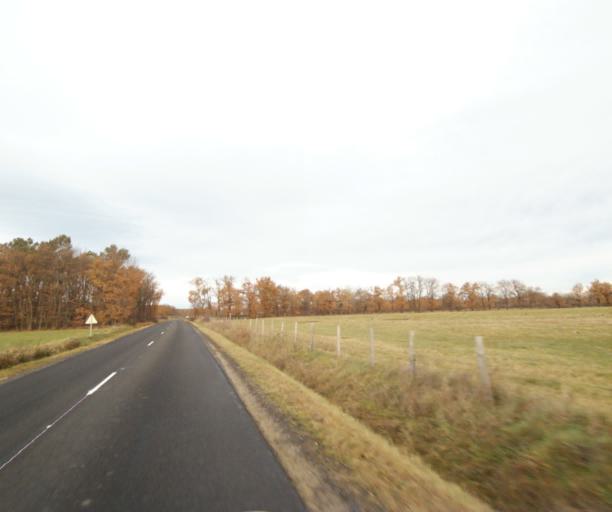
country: FR
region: Rhone-Alpes
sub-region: Departement de la Loire
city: Sury-le-Comtal
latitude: 45.5290
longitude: 4.1582
